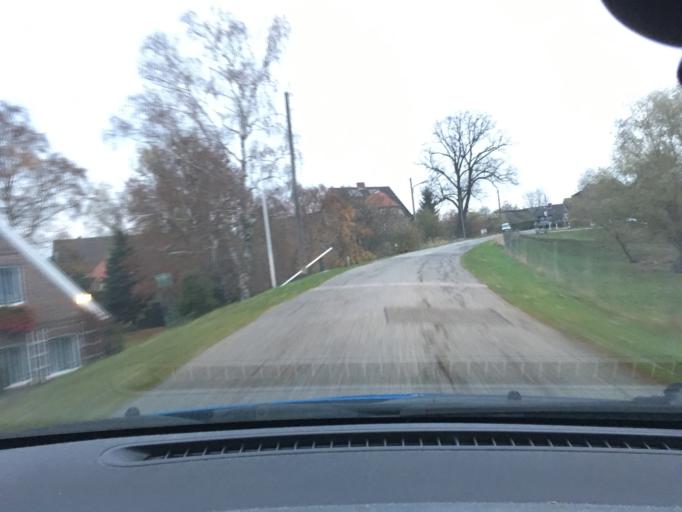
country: DE
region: Lower Saxony
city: Drage
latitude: 53.4271
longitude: 10.2670
